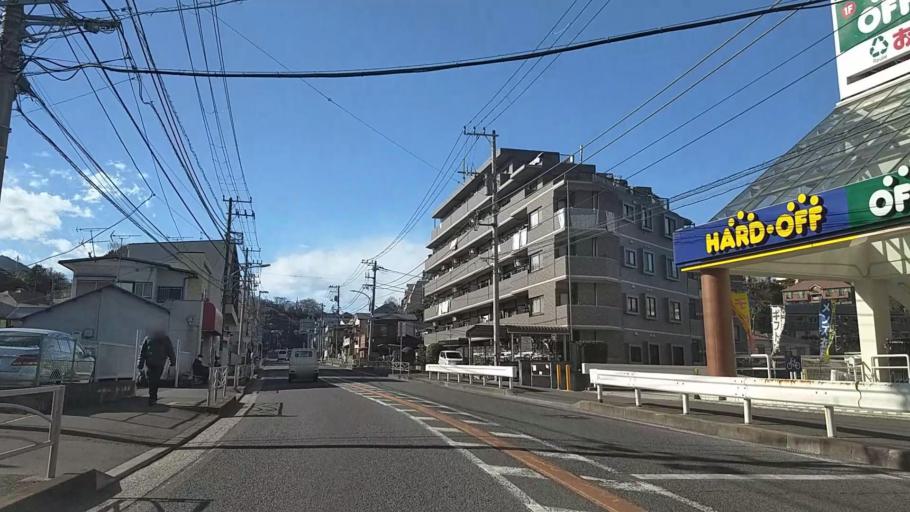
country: JP
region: Kanagawa
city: Yokohama
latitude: 35.3721
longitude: 139.6311
